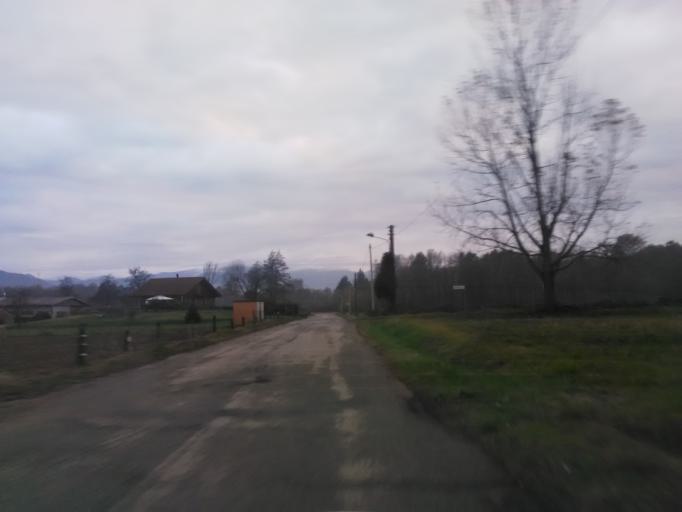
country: IT
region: Piedmont
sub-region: Provincia di Novara
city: Prato Sesia
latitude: 45.6621
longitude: 8.3754
